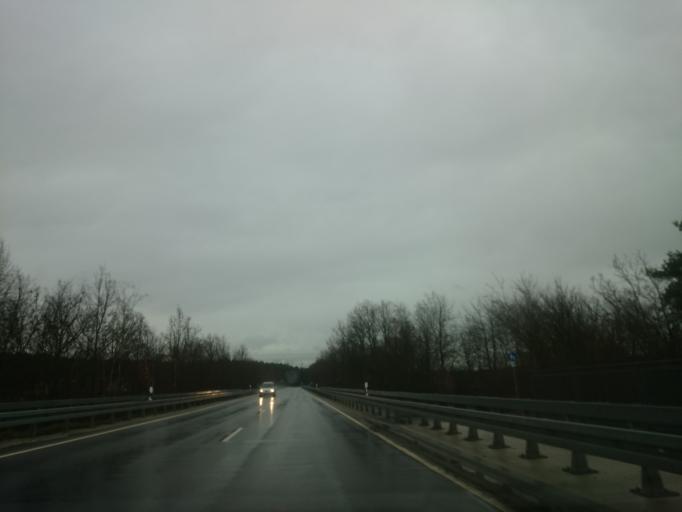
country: DE
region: Bavaria
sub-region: Regierungsbezirk Mittelfranken
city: Hilpoltstein
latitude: 49.1983
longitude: 11.2057
